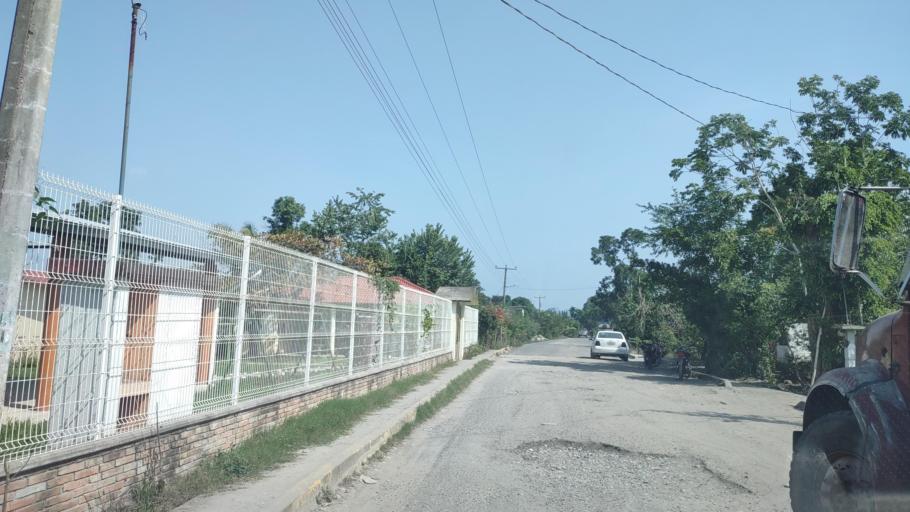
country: MX
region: Puebla
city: Espinal
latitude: 20.2525
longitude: -97.3355
